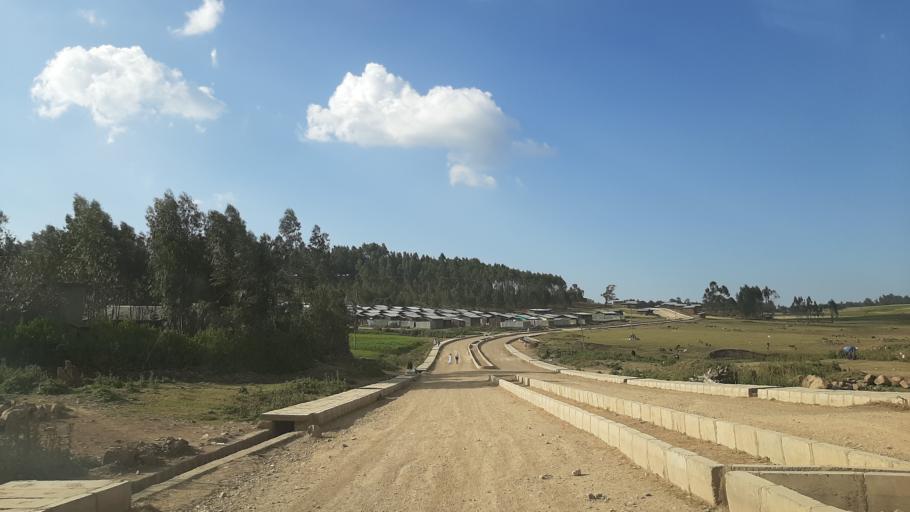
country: ET
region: Amhara
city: Dabat
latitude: 12.9876
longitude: 37.7665
